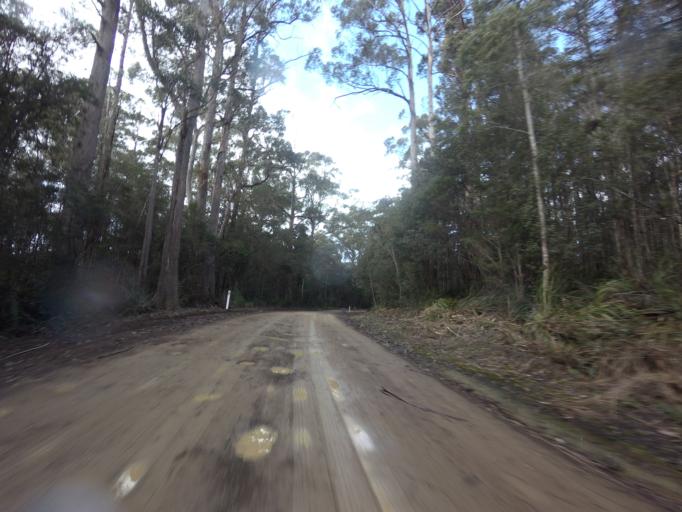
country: AU
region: Tasmania
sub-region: Huon Valley
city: Geeveston
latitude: -43.5752
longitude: 146.8882
